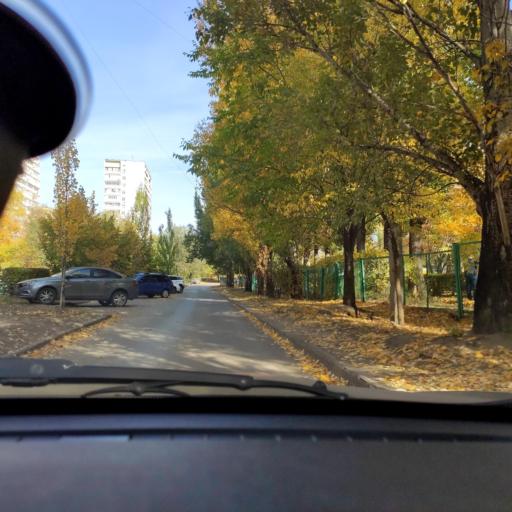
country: RU
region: Samara
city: Tol'yatti
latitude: 53.5238
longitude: 49.3063
